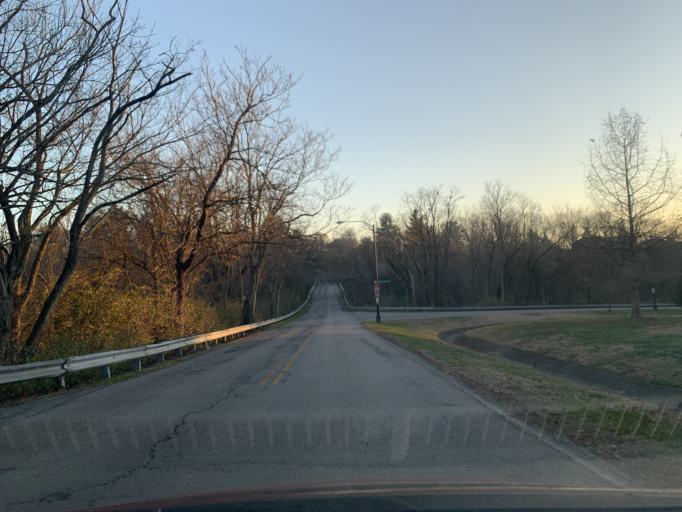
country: US
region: Kentucky
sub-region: Jefferson County
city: Saint Matthews
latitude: 38.2438
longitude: -85.6875
